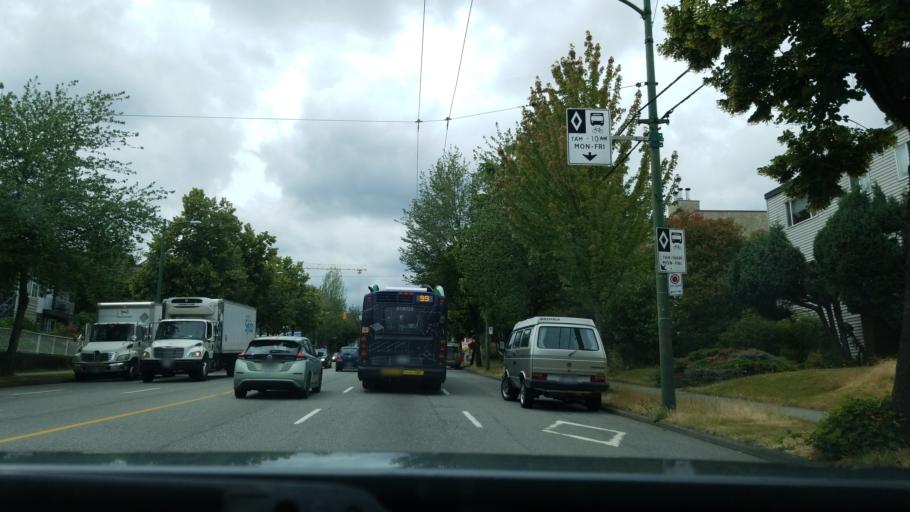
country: CA
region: British Columbia
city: Vancouver
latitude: 49.2624
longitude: -123.0858
